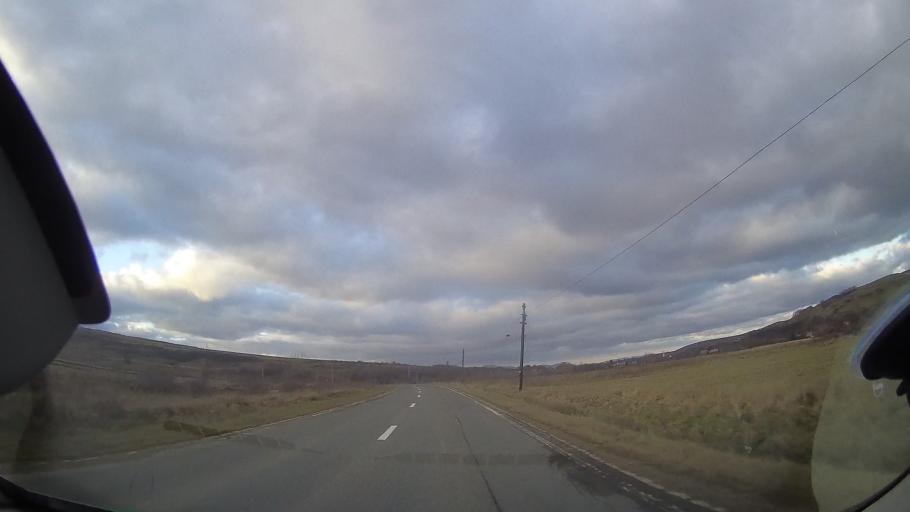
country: RO
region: Cluj
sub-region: Comuna Calatele
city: Calatele
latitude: 46.7918
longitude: 22.9973
